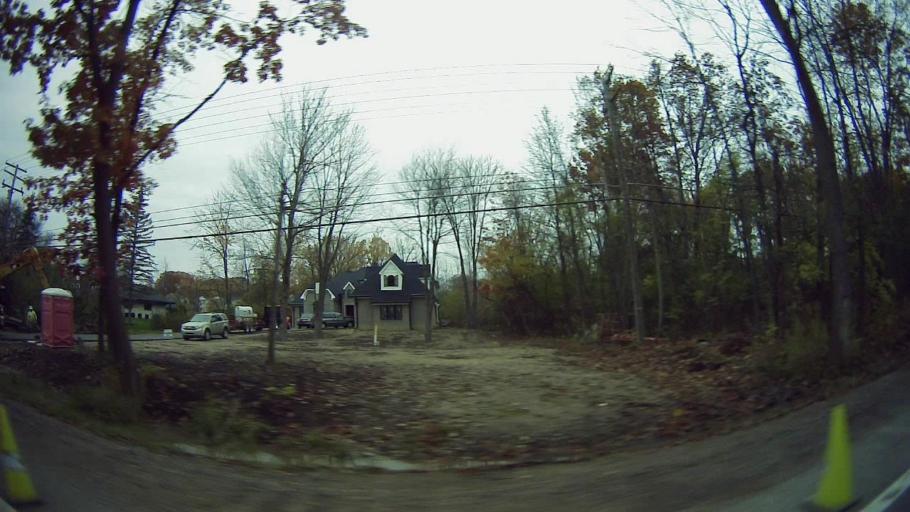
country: US
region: Michigan
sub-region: Oakland County
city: Franklin
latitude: 42.5155
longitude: -83.2904
